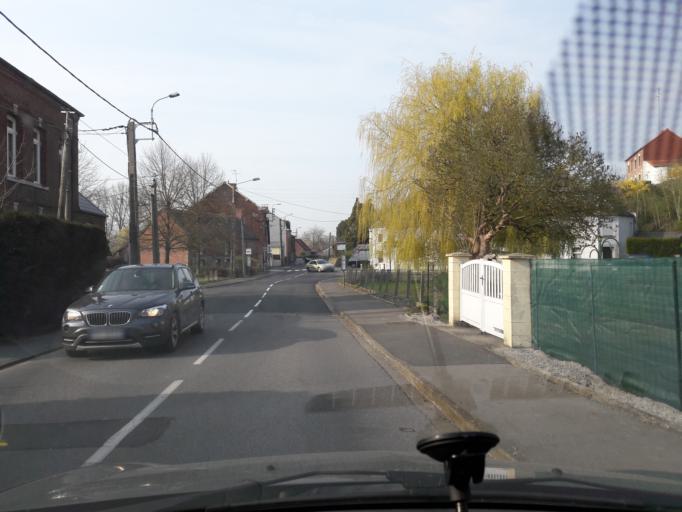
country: FR
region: Nord-Pas-de-Calais
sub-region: Departement du Nord
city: Rousies
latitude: 50.2691
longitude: 4.0048
